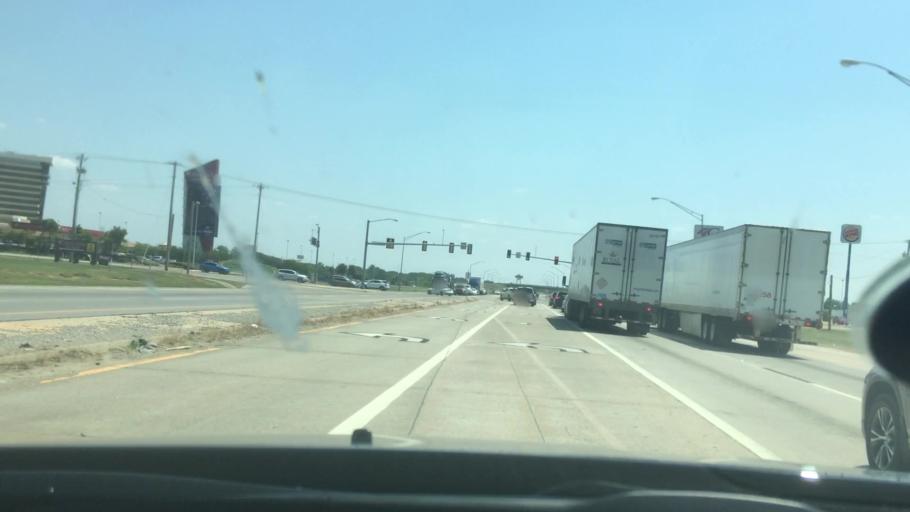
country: US
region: Oklahoma
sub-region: Bryan County
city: Calera
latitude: 33.9555
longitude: -96.4167
